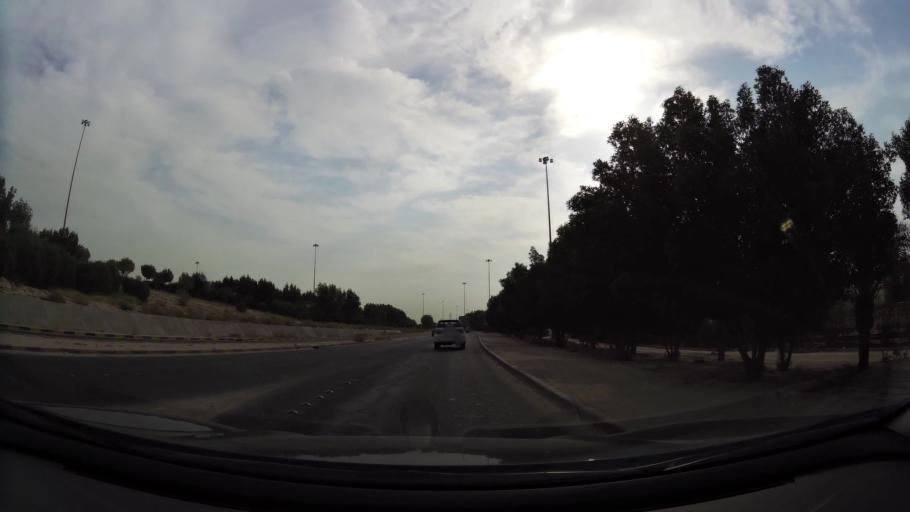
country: KW
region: Muhafazat al Jahra'
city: Al Jahra'
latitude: 29.3223
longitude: 47.7520
